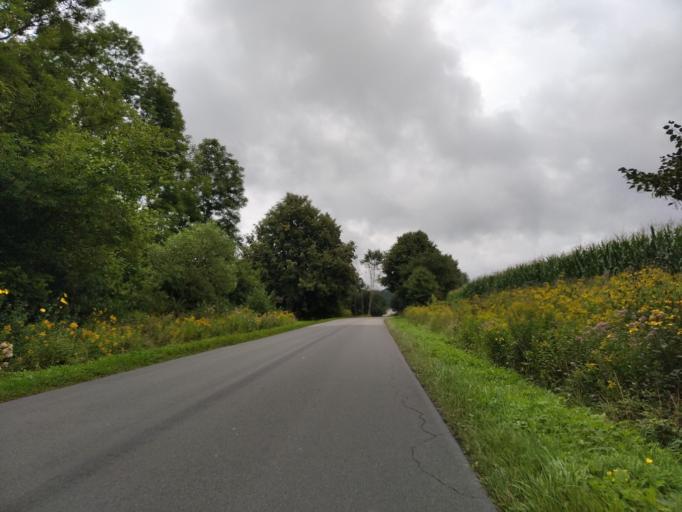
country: PL
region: Subcarpathian Voivodeship
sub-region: Powiat brzozowski
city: Nozdrzec
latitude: 49.7254
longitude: 22.2861
